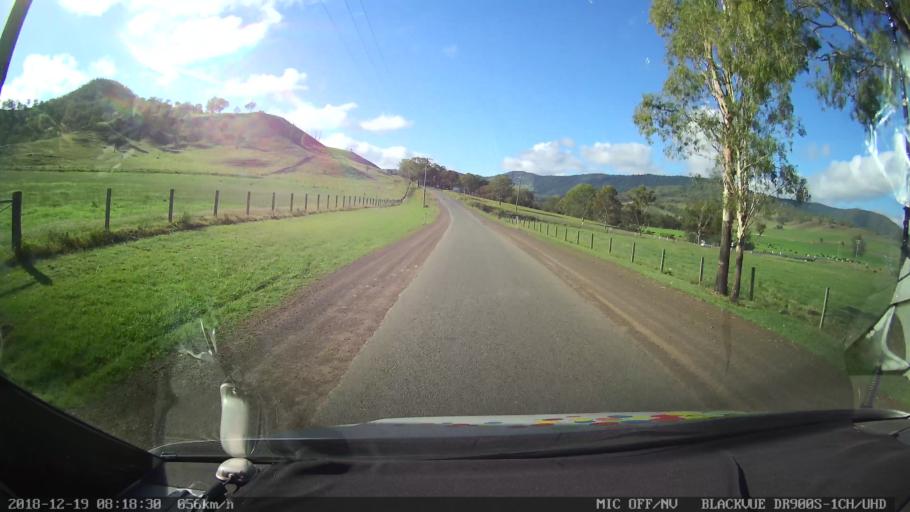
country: AU
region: New South Wales
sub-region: Kyogle
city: Kyogle
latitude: -28.2739
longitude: 152.9089
